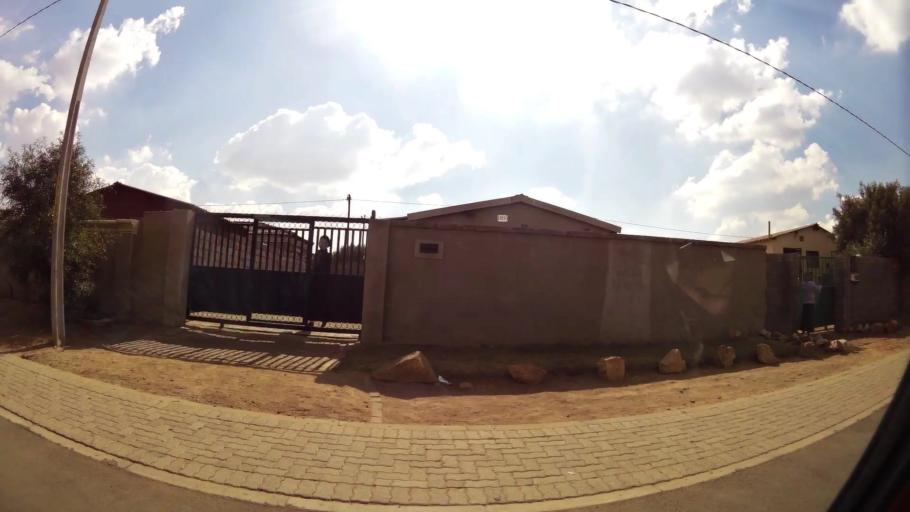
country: ZA
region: Gauteng
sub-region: City of Johannesburg Metropolitan Municipality
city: Roodepoort
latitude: -26.1936
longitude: 27.8735
